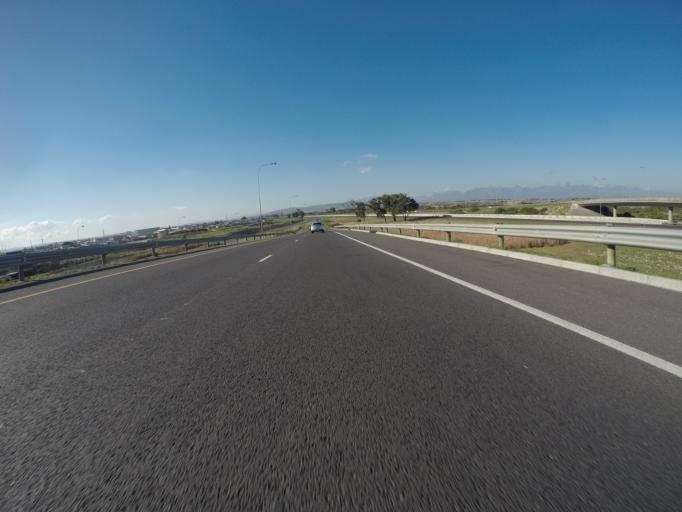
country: ZA
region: Western Cape
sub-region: City of Cape Town
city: Lansdowne
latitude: -33.9988
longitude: 18.6340
